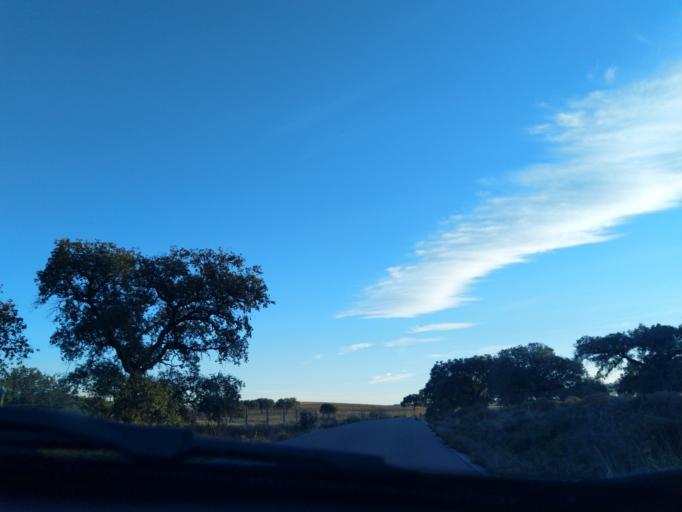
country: ES
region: Extremadura
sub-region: Provincia de Badajoz
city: Valverde de Llerena
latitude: 38.2331
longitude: -5.8223
